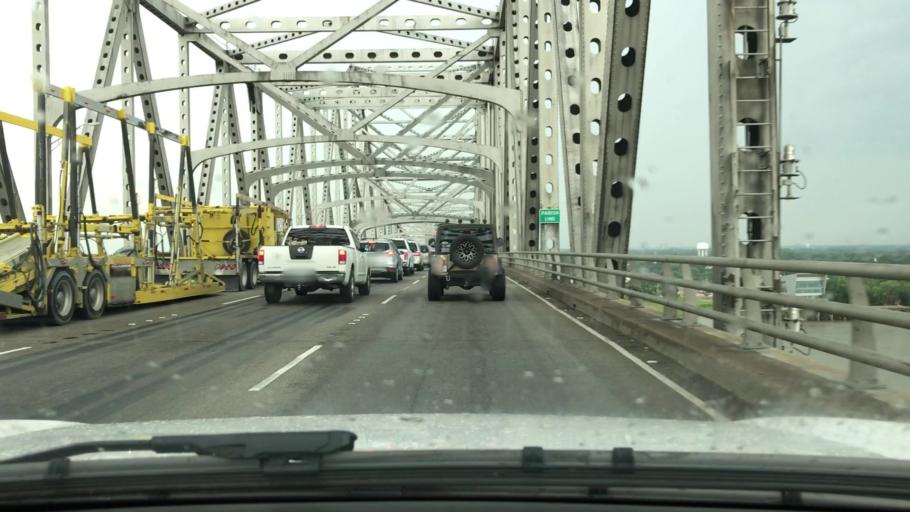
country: US
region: Louisiana
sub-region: West Baton Rouge Parish
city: Port Allen
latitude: 30.4396
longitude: -91.1989
